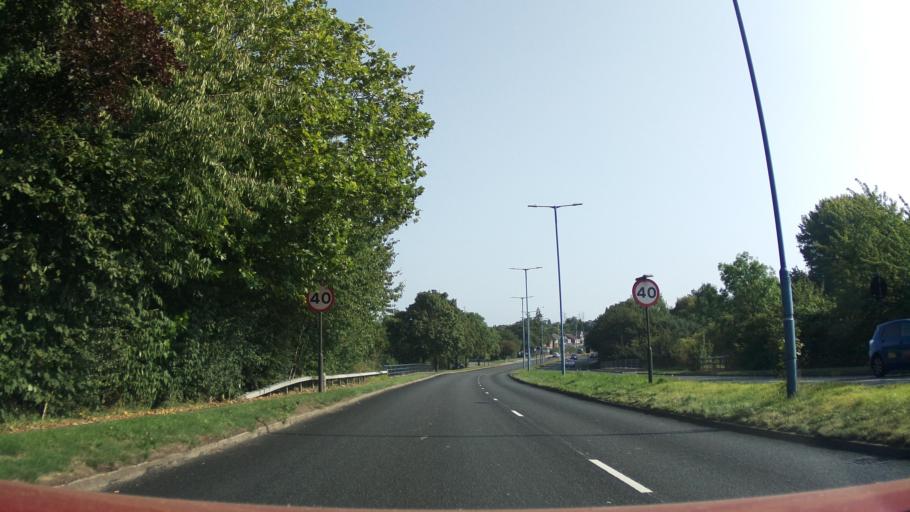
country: GB
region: England
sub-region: Sandwell
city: West Bromwich
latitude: 52.5409
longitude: -1.9624
